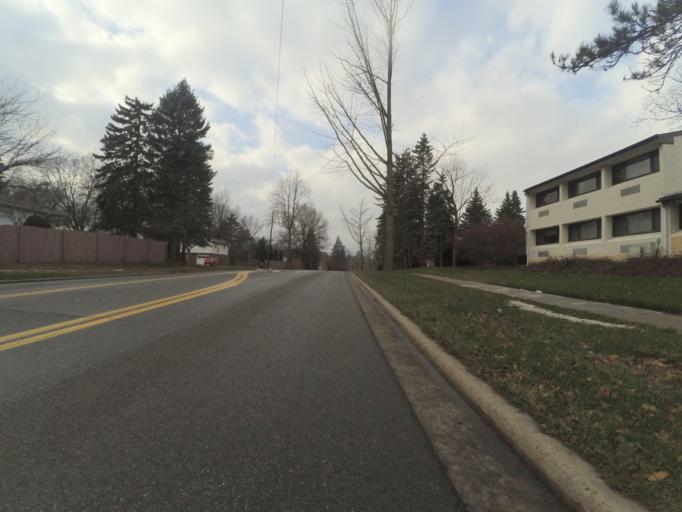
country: US
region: Pennsylvania
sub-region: Centre County
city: State College
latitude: 40.7979
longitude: -77.8457
